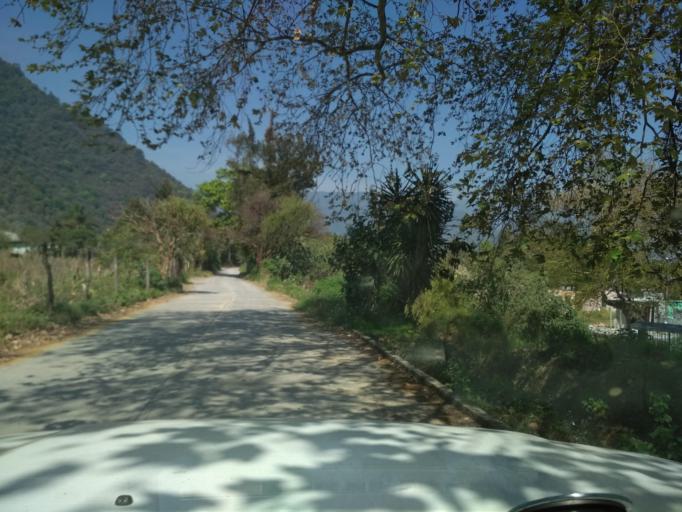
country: MX
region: Veracruz
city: Jalapilla
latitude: 18.8207
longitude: -97.0913
